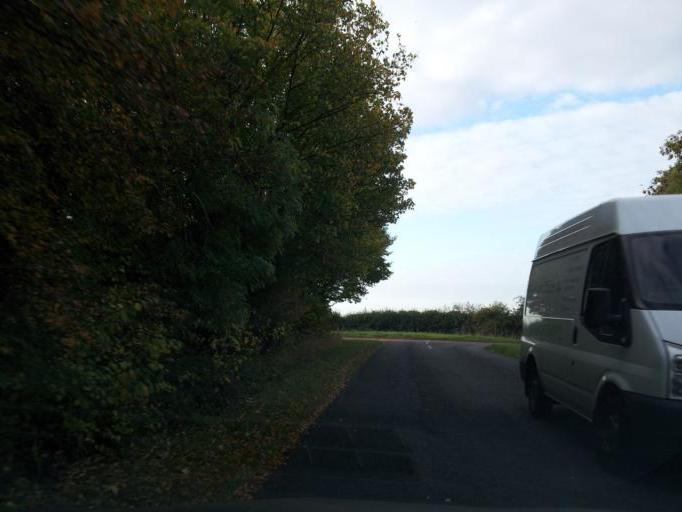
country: GB
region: England
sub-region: Lincolnshire
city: Long Bennington
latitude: 52.9832
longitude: -0.7835
